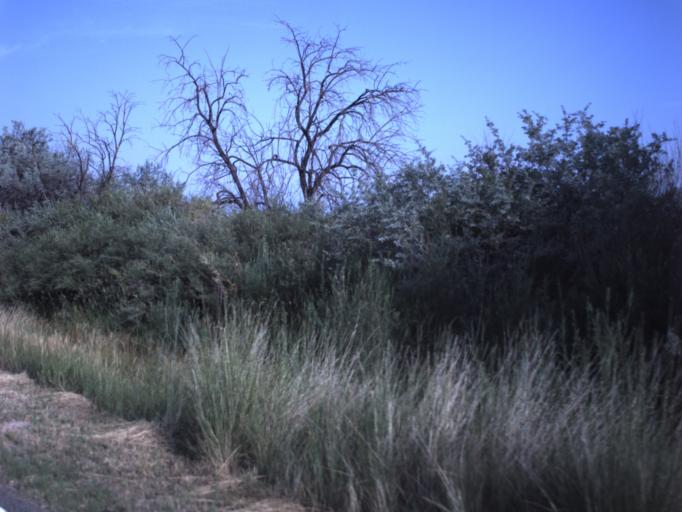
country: US
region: Utah
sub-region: Duchesne County
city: Roosevelt
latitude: 40.2580
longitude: -110.1953
